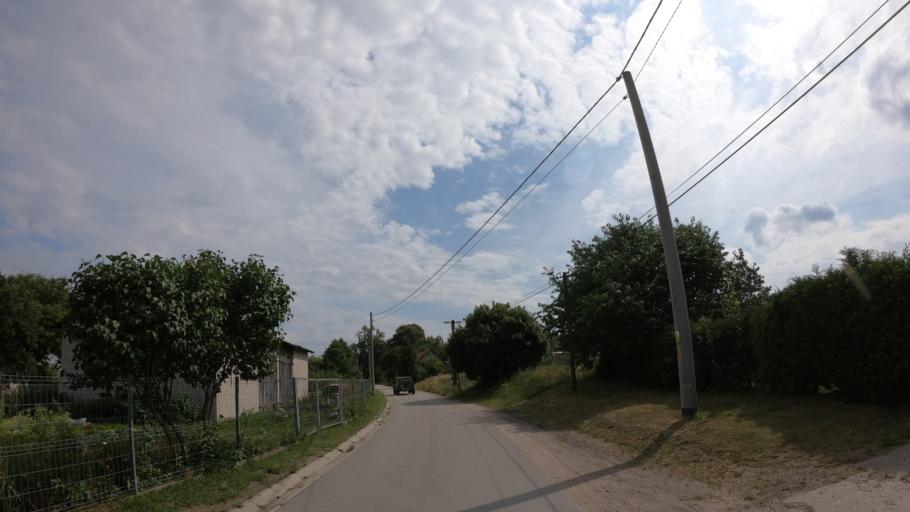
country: PL
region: West Pomeranian Voivodeship
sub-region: Powiat walecki
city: Tuczno
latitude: 53.2329
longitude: 16.1101
